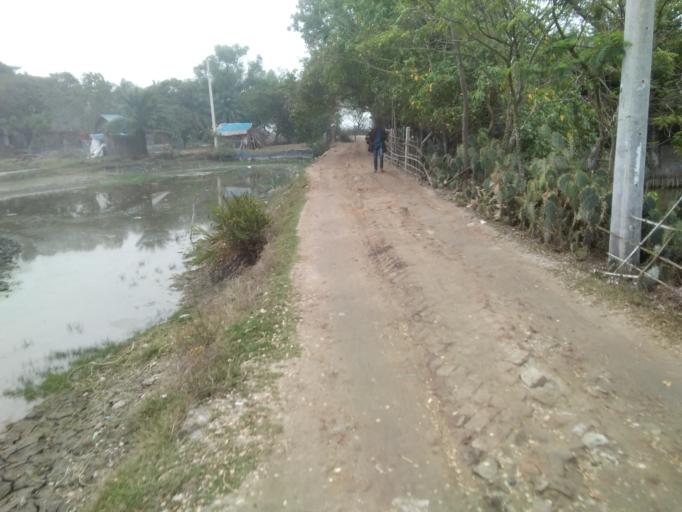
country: BD
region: Khulna
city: Satkhira
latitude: 22.5723
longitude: 89.0770
